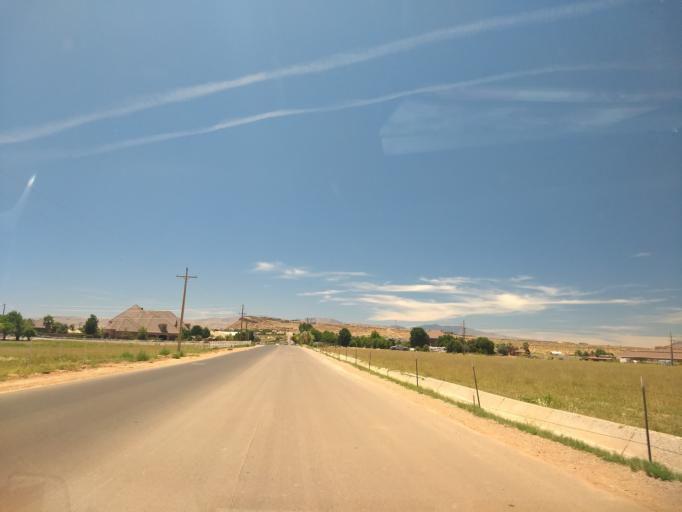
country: US
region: Utah
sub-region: Washington County
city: Washington
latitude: 37.0743
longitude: -113.5114
